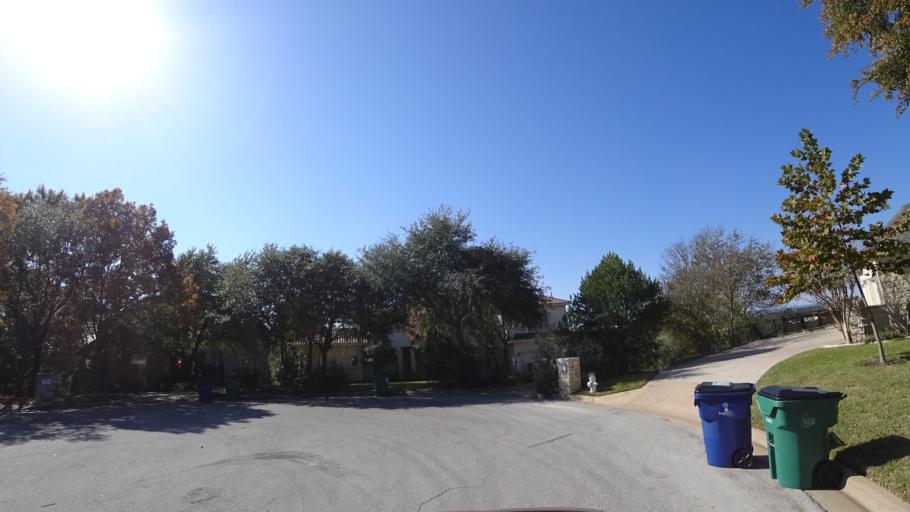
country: US
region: Texas
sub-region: Travis County
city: Lost Creek
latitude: 30.3714
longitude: -97.8462
